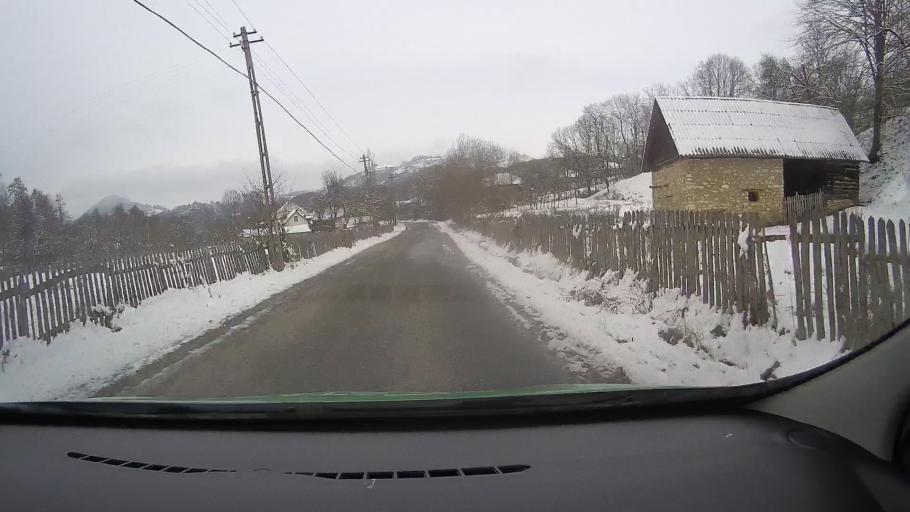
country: RO
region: Alba
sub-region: Comuna Almasu Mare
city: Almasu Mare
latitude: 46.0960
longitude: 23.1294
